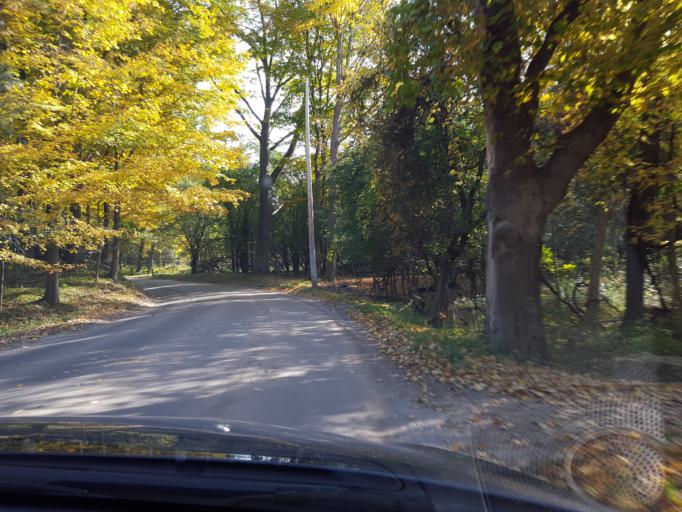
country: CA
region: Ontario
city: Ancaster
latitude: 43.2380
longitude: -80.0013
